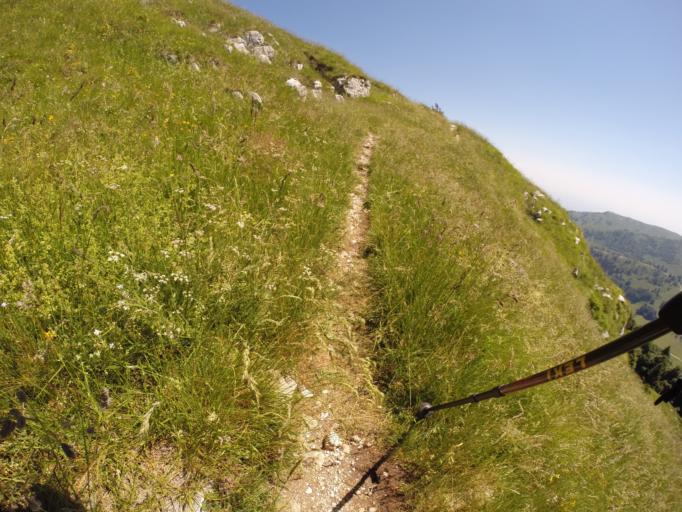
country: IT
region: Veneto
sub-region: Provincia di Treviso
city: Crespano del Grappa
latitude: 45.9006
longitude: 11.8192
